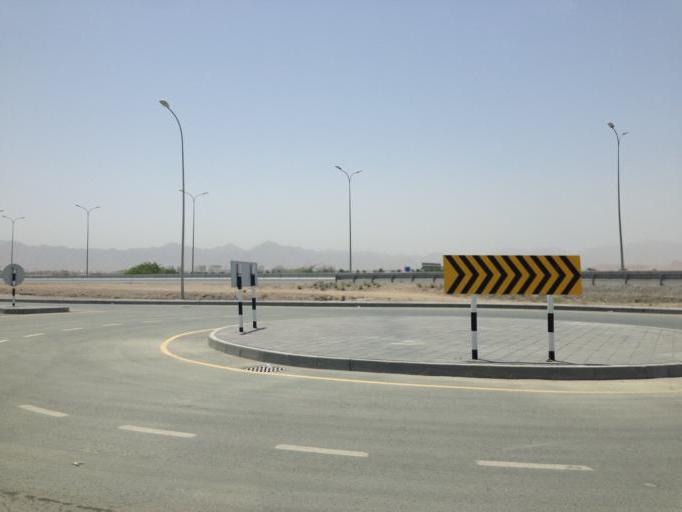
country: OM
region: Muhafazat Masqat
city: Bawshar
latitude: 23.6066
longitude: 58.3213
